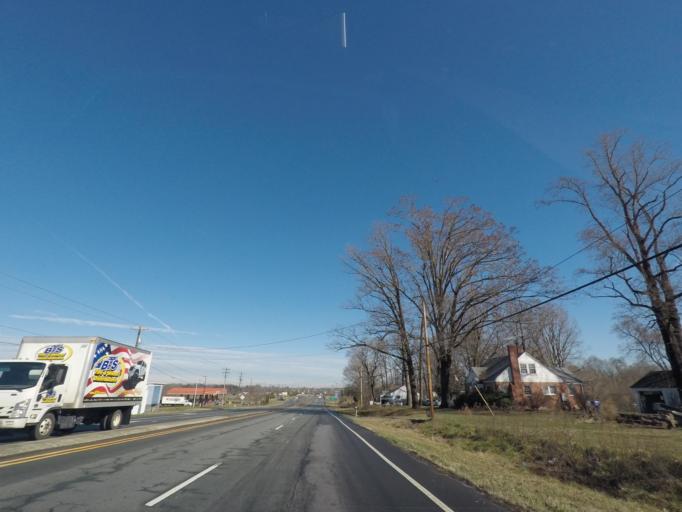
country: US
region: North Carolina
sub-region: Guilford County
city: Pleasant Garden
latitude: 35.9975
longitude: -79.7920
